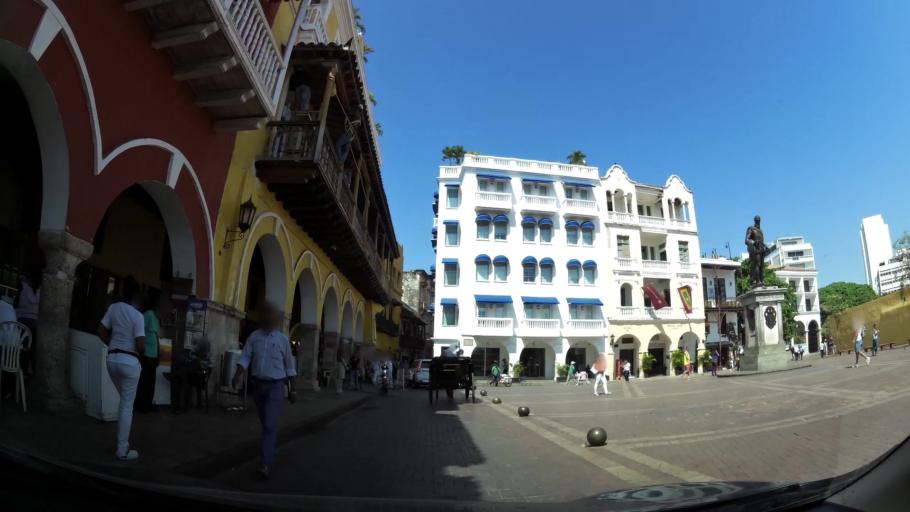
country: CO
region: Bolivar
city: Cartagena
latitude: 10.4231
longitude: -75.5494
